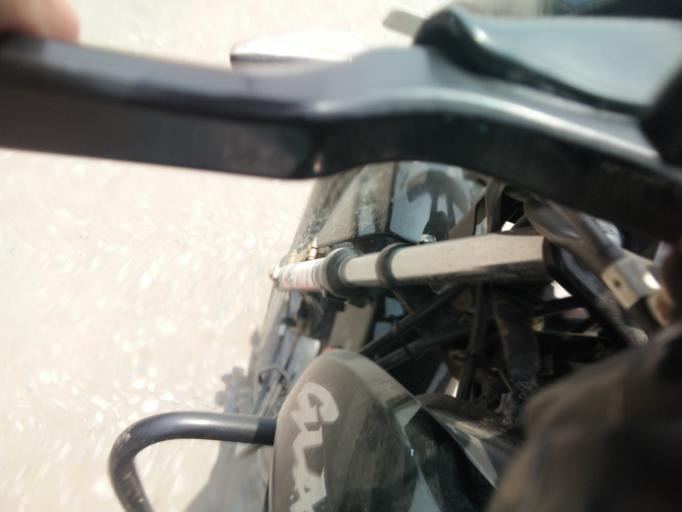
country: IN
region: Uttar Pradesh
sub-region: Ghazipur
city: Zamania
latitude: 25.4339
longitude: 83.6732
